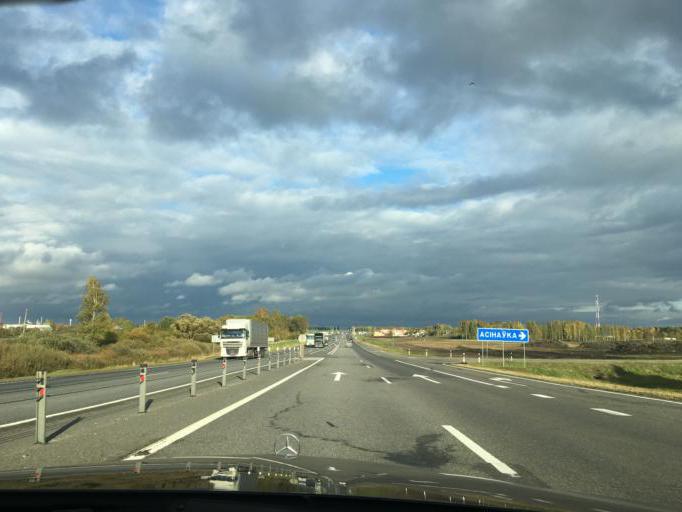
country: BY
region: Vitebsk
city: Dubrowna
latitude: 54.6559
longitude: 30.6489
